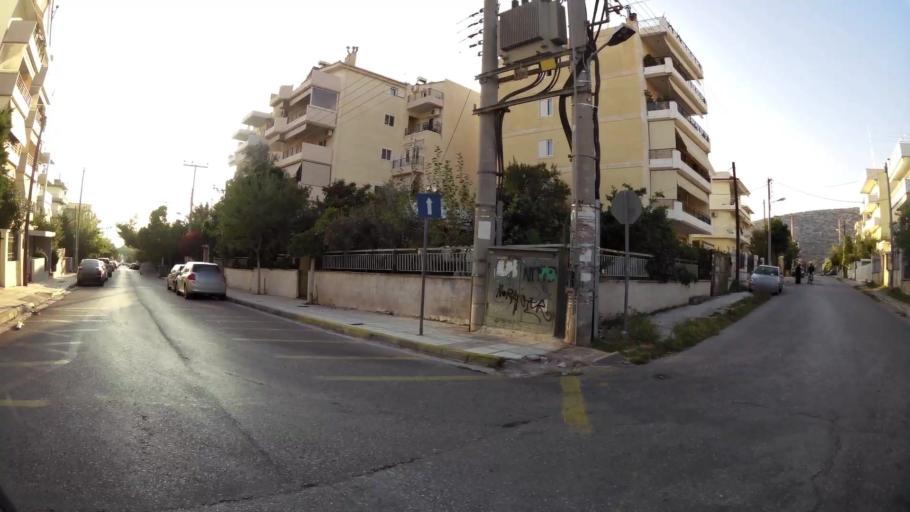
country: GR
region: Attica
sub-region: Nomarchia Athinas
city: Argyroupoli
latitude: 37.8990
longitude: 23.7731
